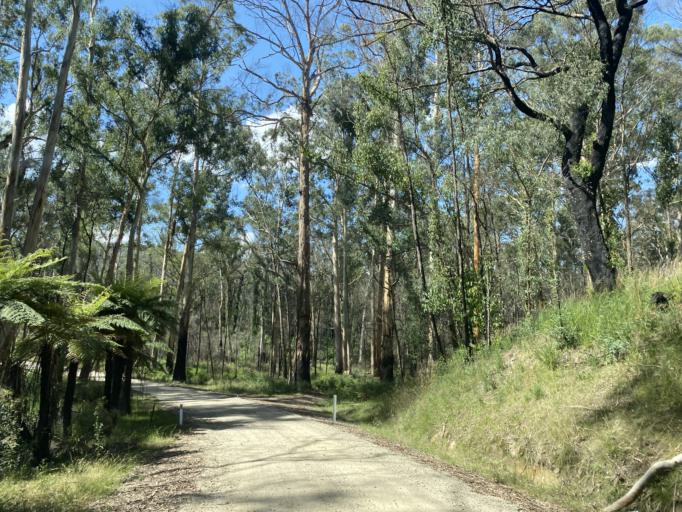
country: AU
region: Victoria
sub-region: Cardinia
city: Gembrook
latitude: -37.9810
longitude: 145.6229
